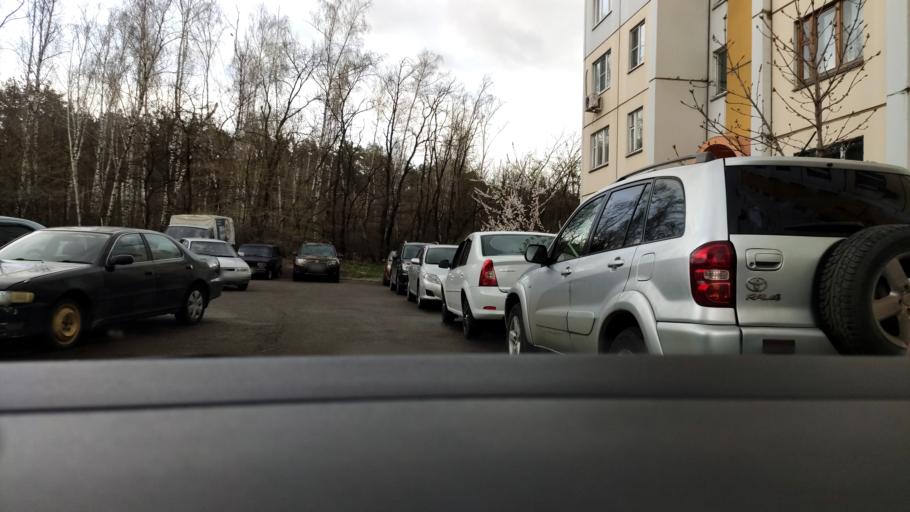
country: RU
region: Voronezj
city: Pridonskoy
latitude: 51.6521
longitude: 39.1025
